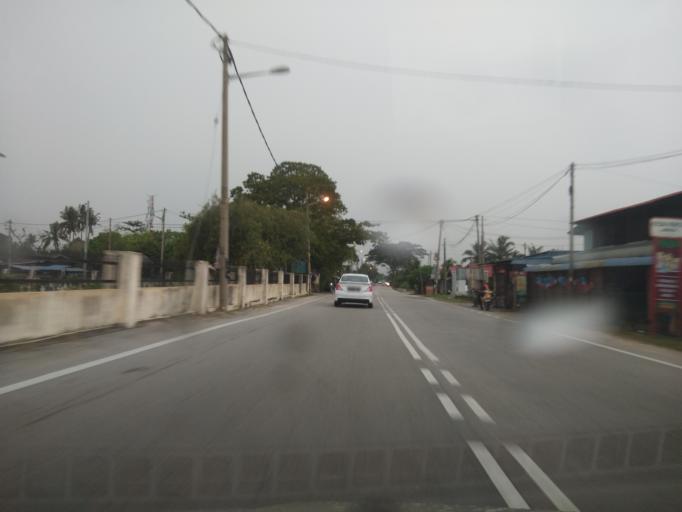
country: MY
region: Penang
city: Permatang Kuching
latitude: 5.4776
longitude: 100.4014
